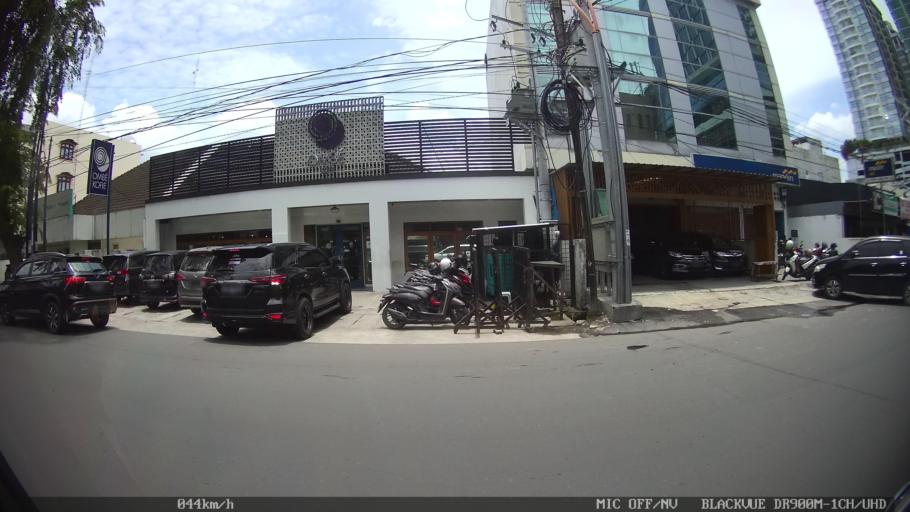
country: ID
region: North Sumatra
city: Medan
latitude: 3.5856
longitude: 98.6671
